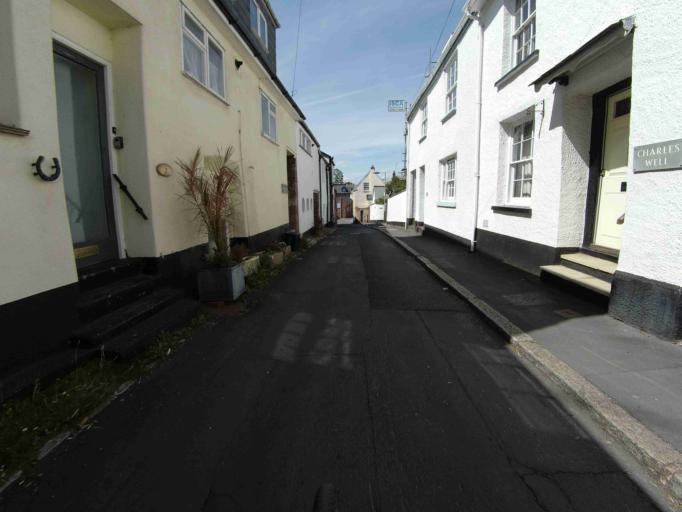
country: GB
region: England
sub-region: Devon
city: Topsham
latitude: 50.6809
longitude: -3.4641
